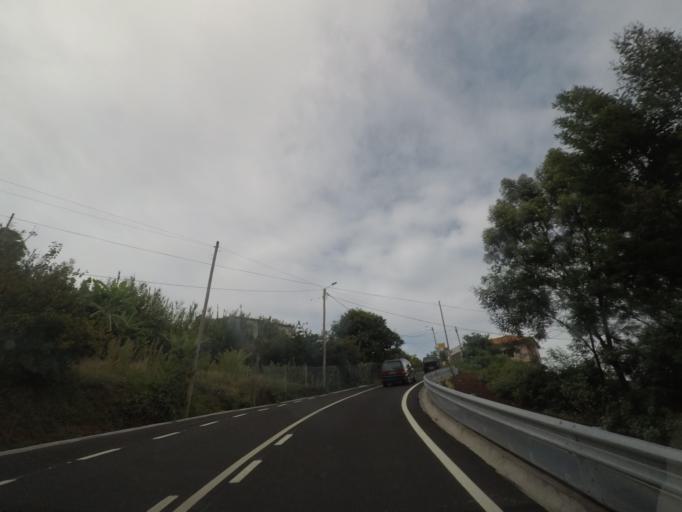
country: PT
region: Madeira
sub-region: Santana
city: Santana
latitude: 32.8309
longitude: -16.9081
